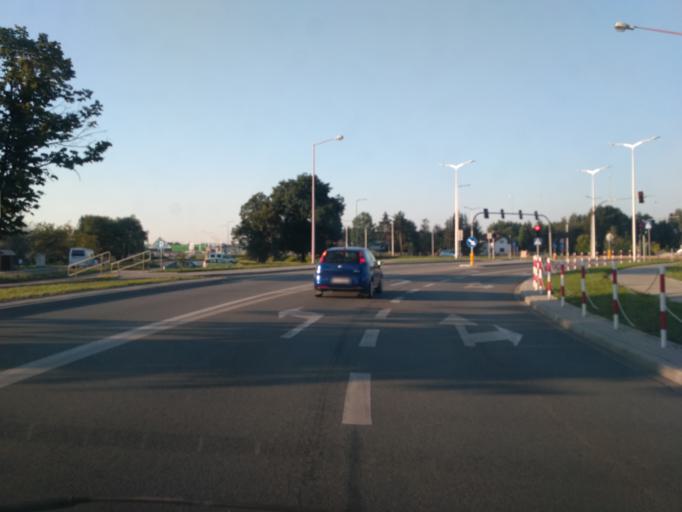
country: PL
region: Subcarpathian Voivodeship
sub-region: Krosno
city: Krosno
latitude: 49.6801
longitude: 21.7728
